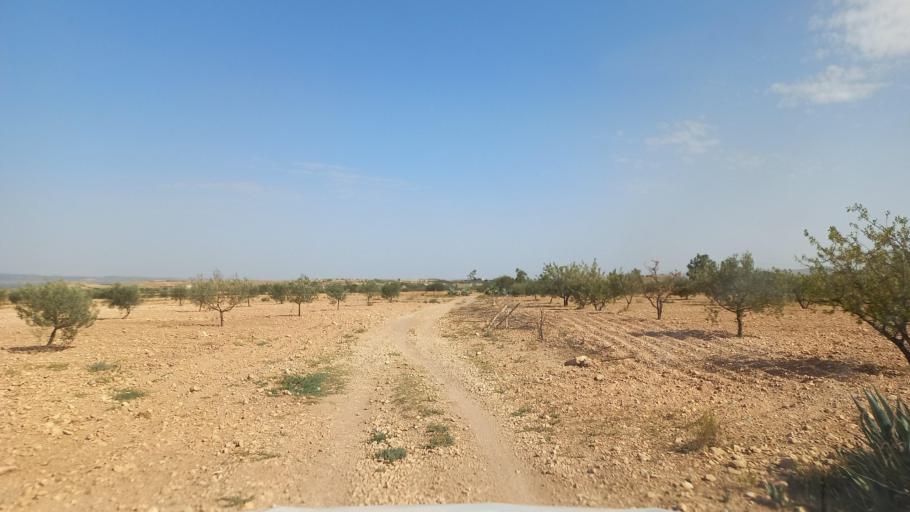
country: TN
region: Al Qasrayn
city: Kasserine
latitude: 35.2819
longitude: 8.9511
